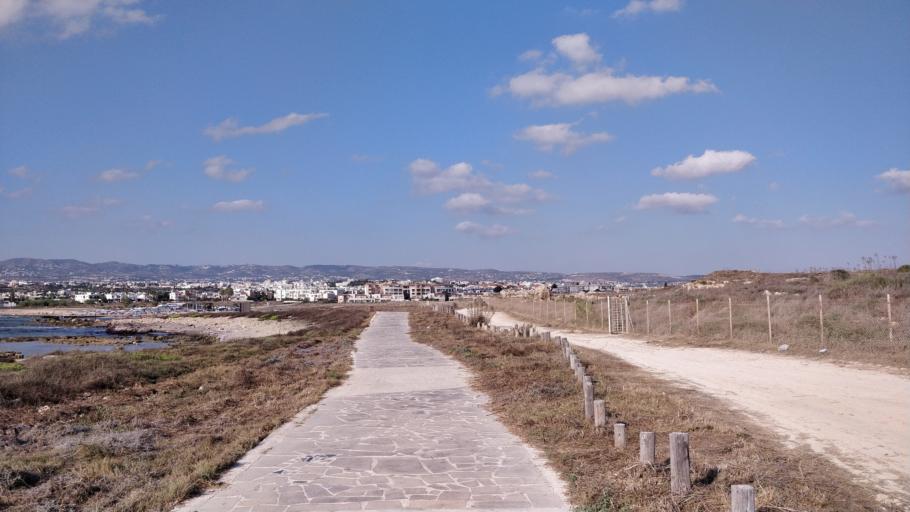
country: CY
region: Pafos
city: Paphos
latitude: 34.7617
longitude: 32.4044
